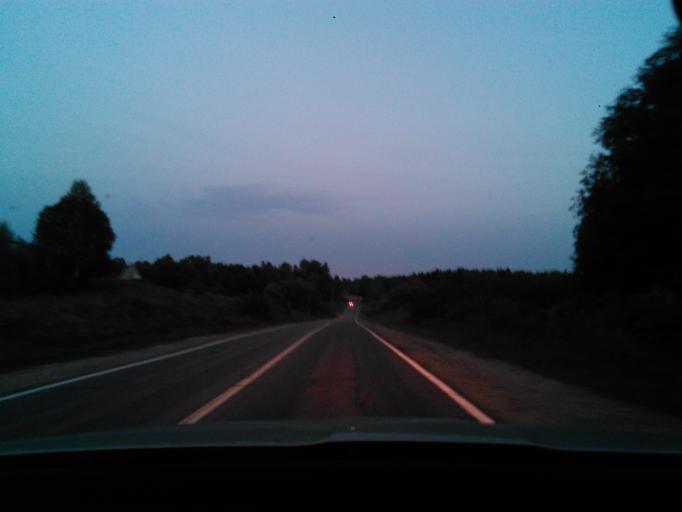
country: RU
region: Moskovskaya
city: Klin
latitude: 56.1506
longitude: 36.7723
